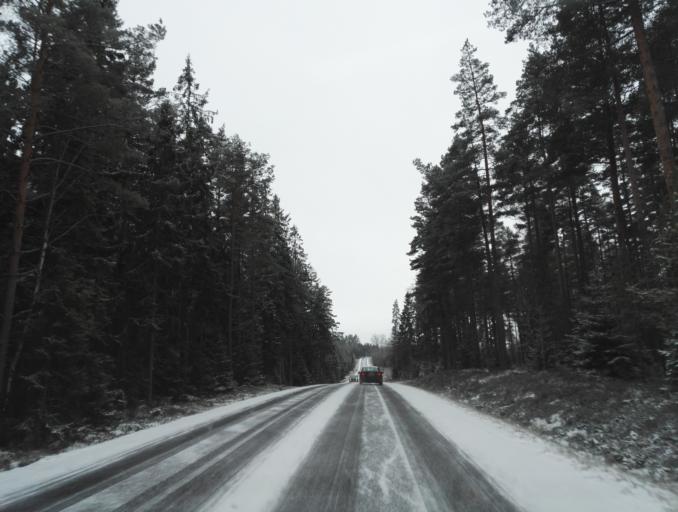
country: SE
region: Kronoberg
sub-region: Lessebo Kommun
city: Lessebo
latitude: 56.7920
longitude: 15.3146
